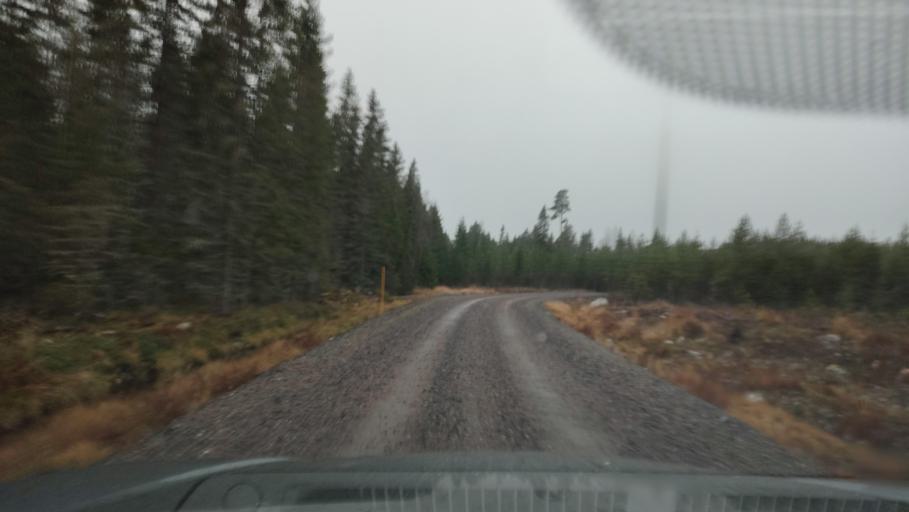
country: FI
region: Southern Ostrobothnia
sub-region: Suupohja
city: Karijoki
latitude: 62.1778
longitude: 21.7200
